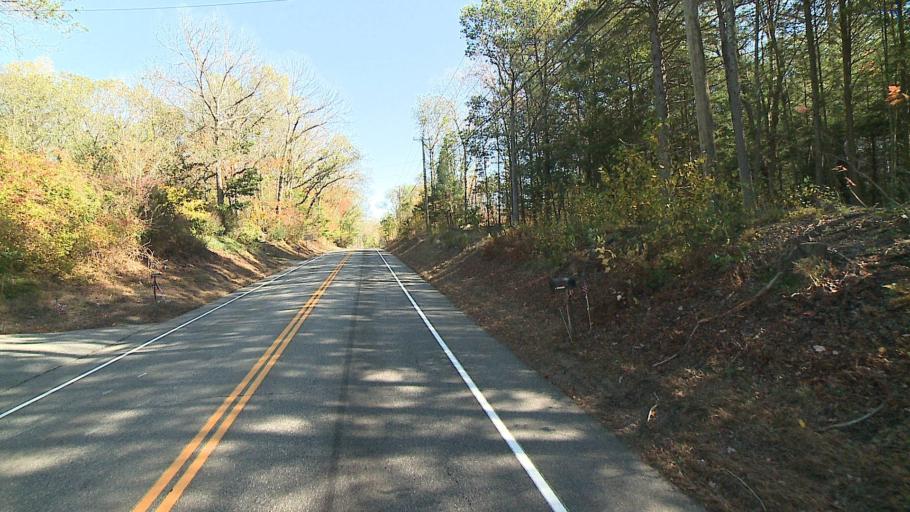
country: US
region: Connecticut
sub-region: Tolland County
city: Storrs
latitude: 41.8655
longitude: -72.1564
